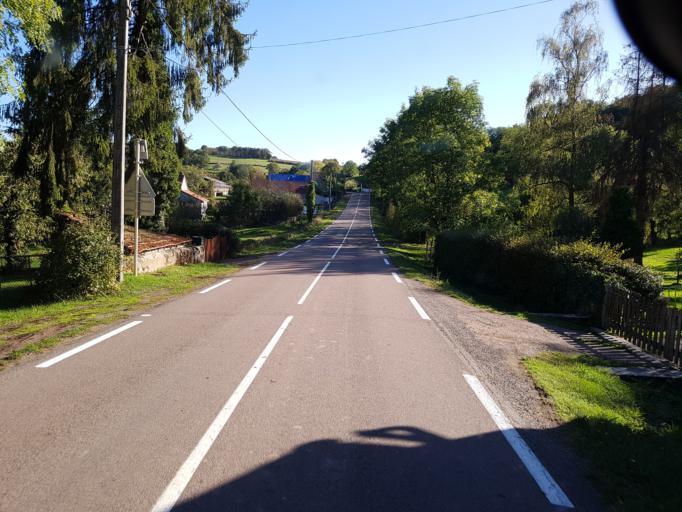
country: FR
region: Bourgogne
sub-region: Departement de Saone-et-Loire
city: Autun
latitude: 47.0532
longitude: 4.2665
